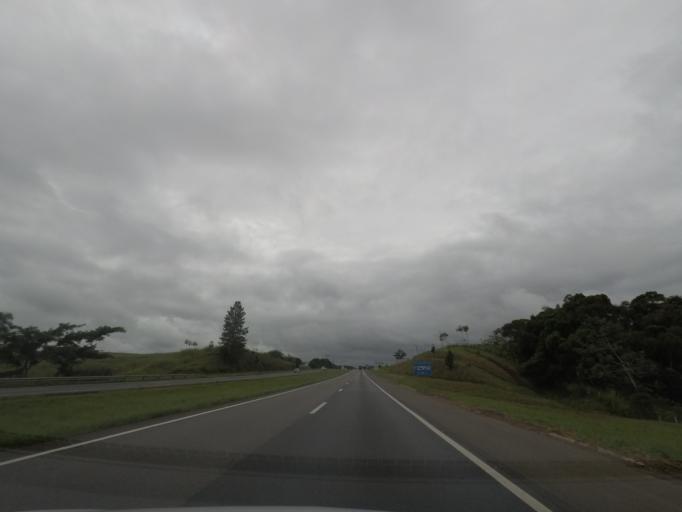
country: BR
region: Sao Paulo
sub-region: Pariquera-Acu
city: Pariquera Acu
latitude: -24.6375
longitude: -47.9113
